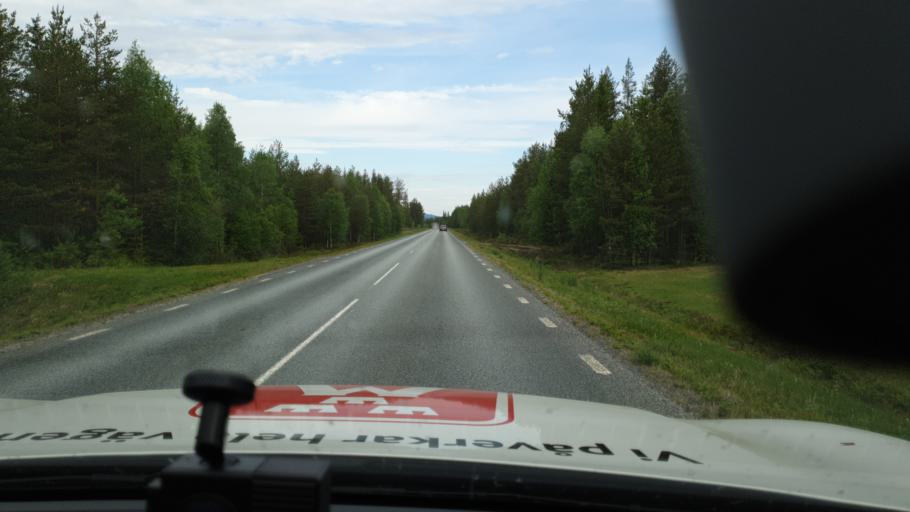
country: SE
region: Vaesterbotten
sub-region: Mala Kommun
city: Mala
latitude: 64.9955
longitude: 18.4843
